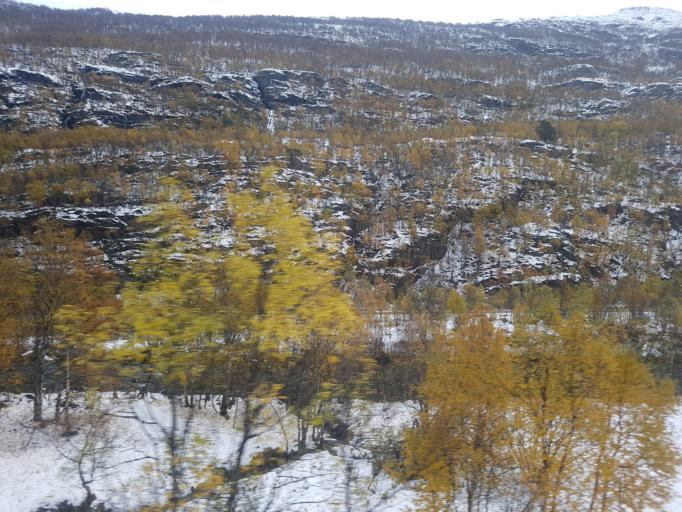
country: NO
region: Sor-Trondelag
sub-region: Oppdal
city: Oppdal
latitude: 62.3991
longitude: 9.6356
